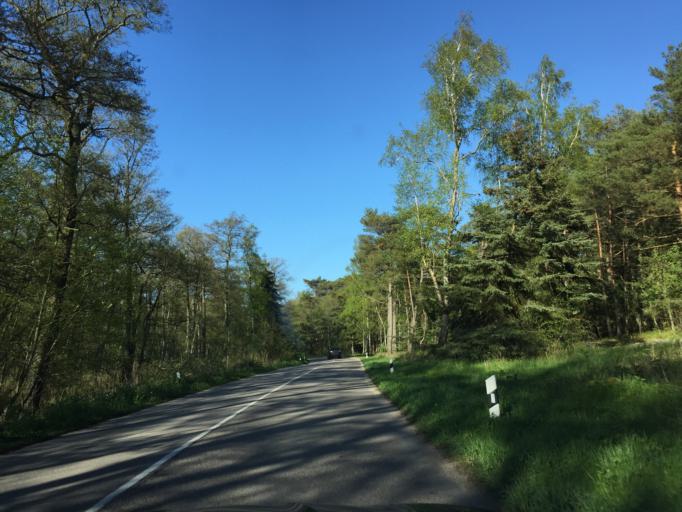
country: LT
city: Nida
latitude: 55.1920
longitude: 20.8603
